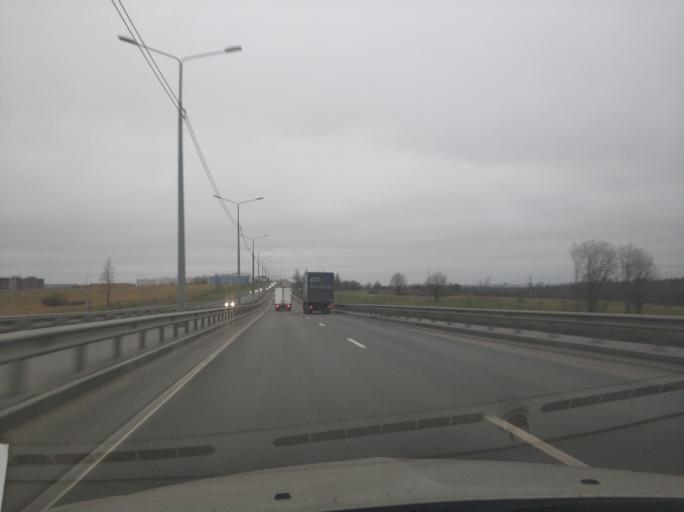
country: RU
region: St.-Petersburg
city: Pushkin
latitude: 59.7565
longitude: 30.3814
